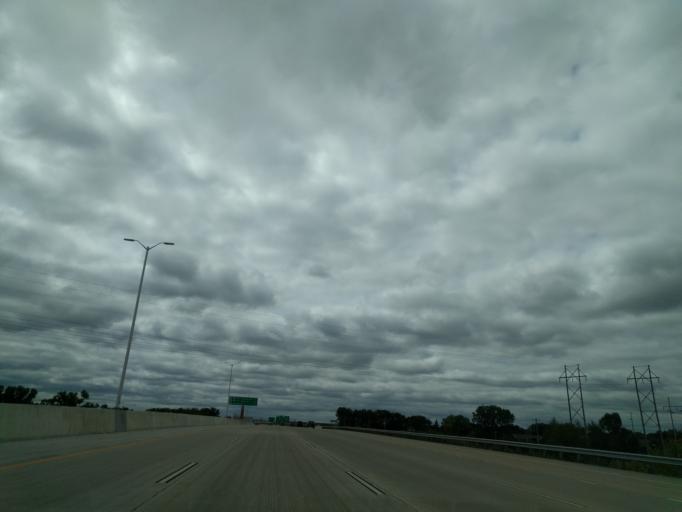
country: US
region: Wisconsin
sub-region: Brown County
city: Howard
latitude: 44.5504
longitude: -88.0674
